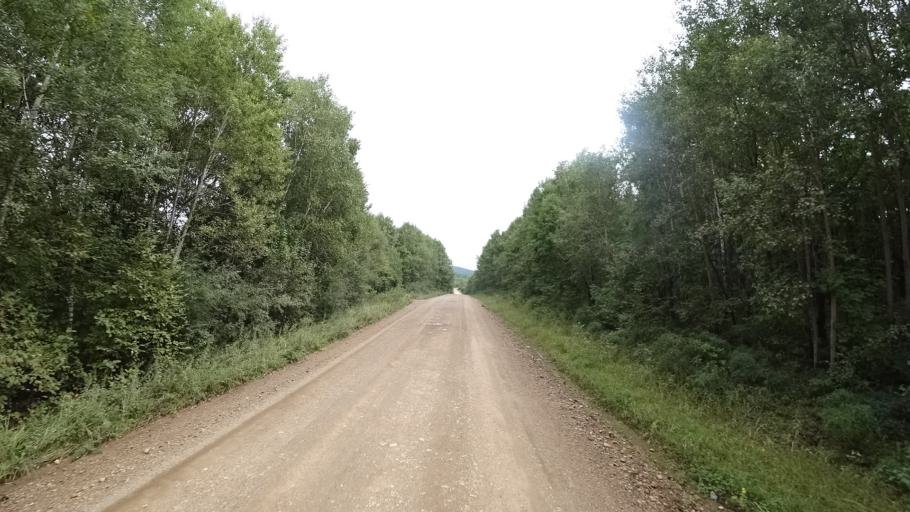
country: RU
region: Primorskiy
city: Lyalichi
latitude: 44.0855
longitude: 132.4414
